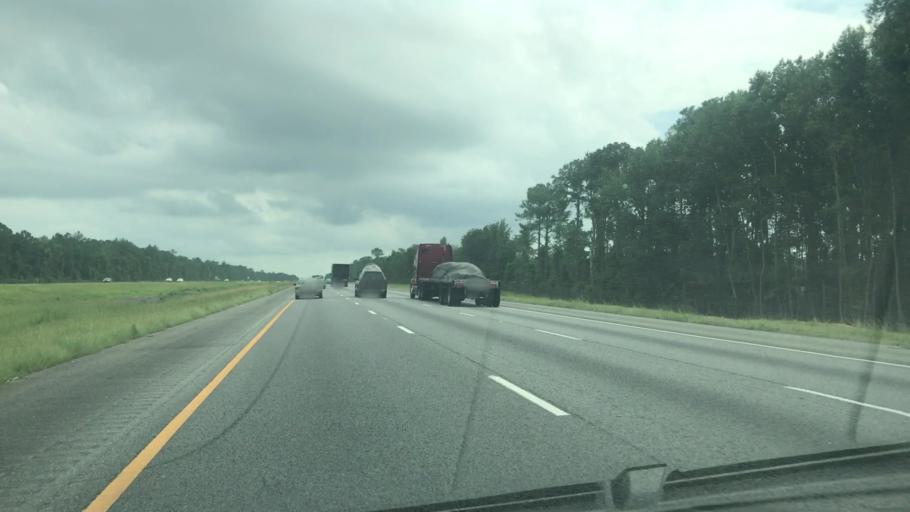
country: US
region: Georgia
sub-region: Glynn County
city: Brunswick
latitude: 31.0787
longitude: -81.6174
